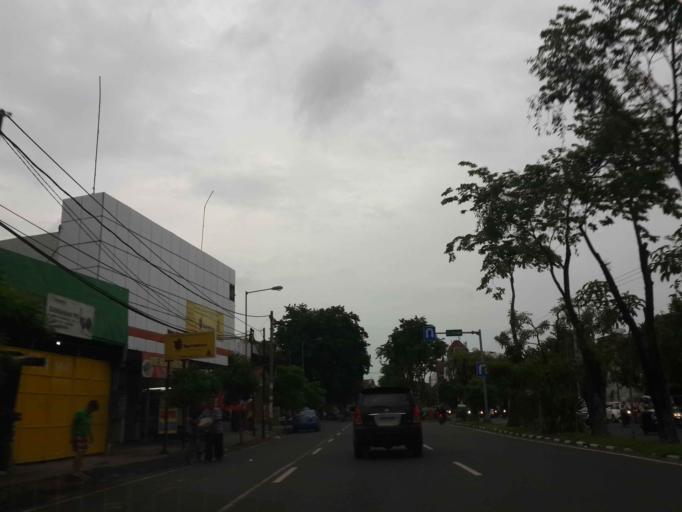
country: ID
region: East Java
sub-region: Kota Surabaya
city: Surabaya
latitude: -7.2672
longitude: 112.7282
